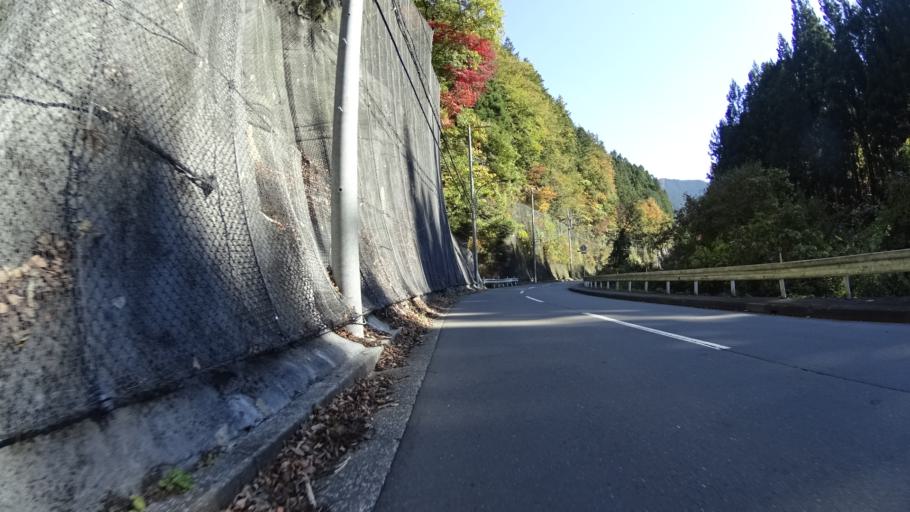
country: JP
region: Yamanashi
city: Uenohara
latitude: 35.7093
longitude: 139.0947
